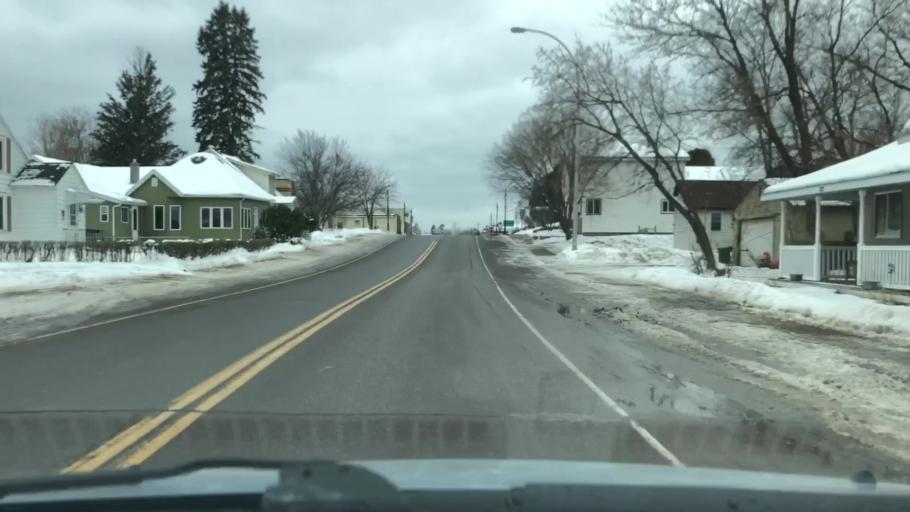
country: US
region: Minnesota
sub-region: Carlton County
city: Carlton
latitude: 46.6640
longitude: -92.4228
